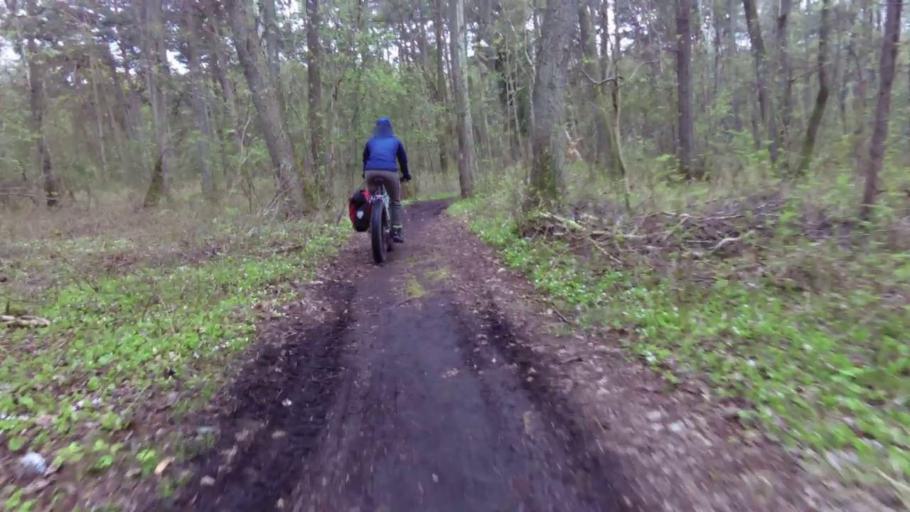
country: PL
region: West Pomeranian Voivodeship
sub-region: Powiat kamienski
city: Dziwnow
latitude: 54.0127
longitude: 14.7039
